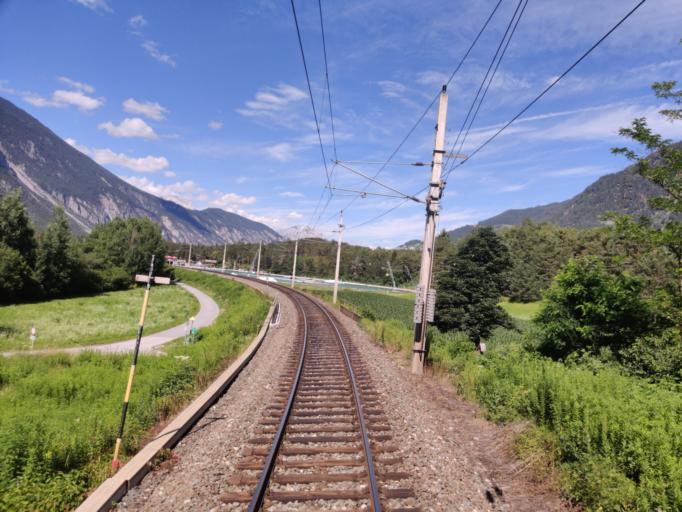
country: AT
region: Tyrol
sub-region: Politischer Bezirk Imst
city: Roppen
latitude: 47.2271
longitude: 10.8359
